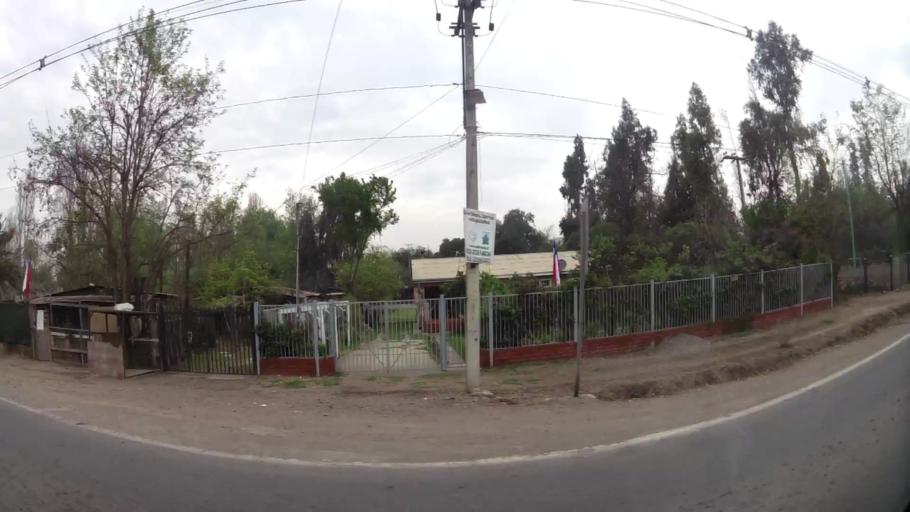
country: CL
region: Santiago Metropolitan
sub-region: Provincia de Chacabuco
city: Chicureo Abajo
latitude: -33.2720
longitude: -70.7465
